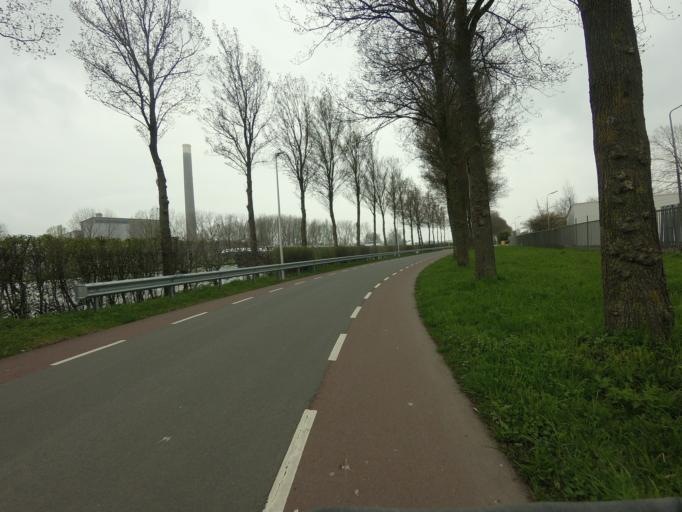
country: NL
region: Utrecht
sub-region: Gemeente Utrecht
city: Utrecht
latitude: 52.1010
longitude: 5.0774
